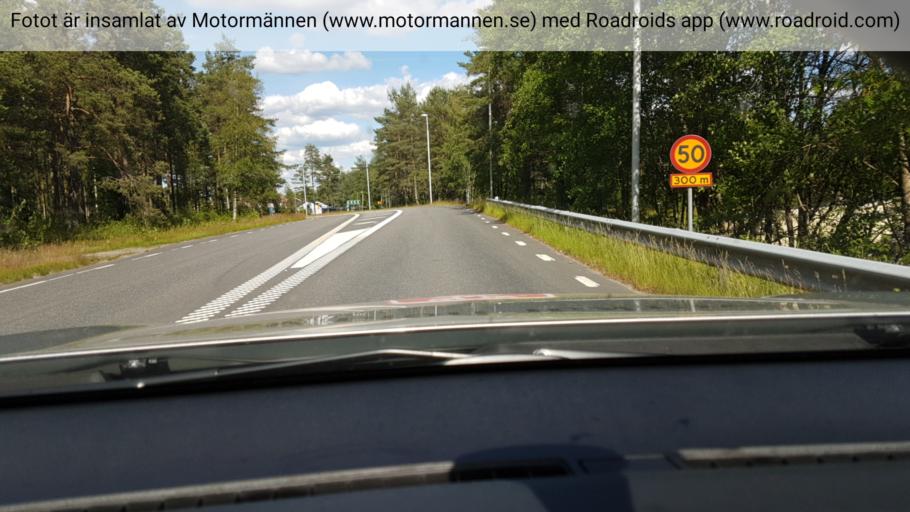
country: SE
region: Joenkoeping
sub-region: Vaggeryds Kommun
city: Vaggeryd
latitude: 57.4861
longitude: 14.1214
